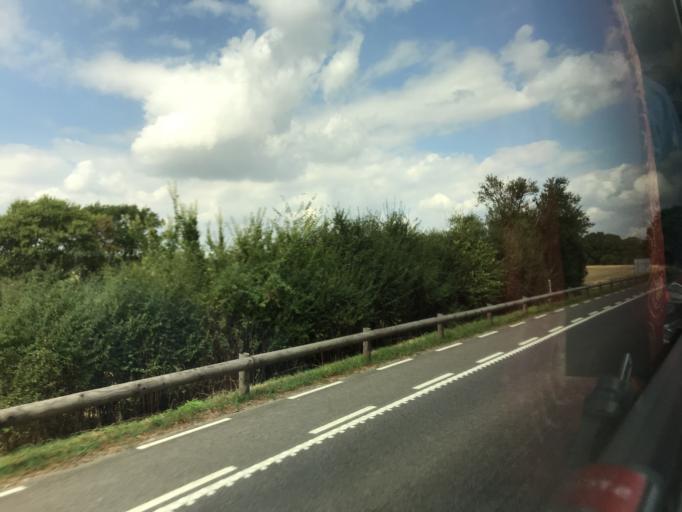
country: LU
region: Luxembourg
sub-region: Canton de Luxembourg
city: Weiler-la-Tour
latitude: 49.5355
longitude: 6.1785
